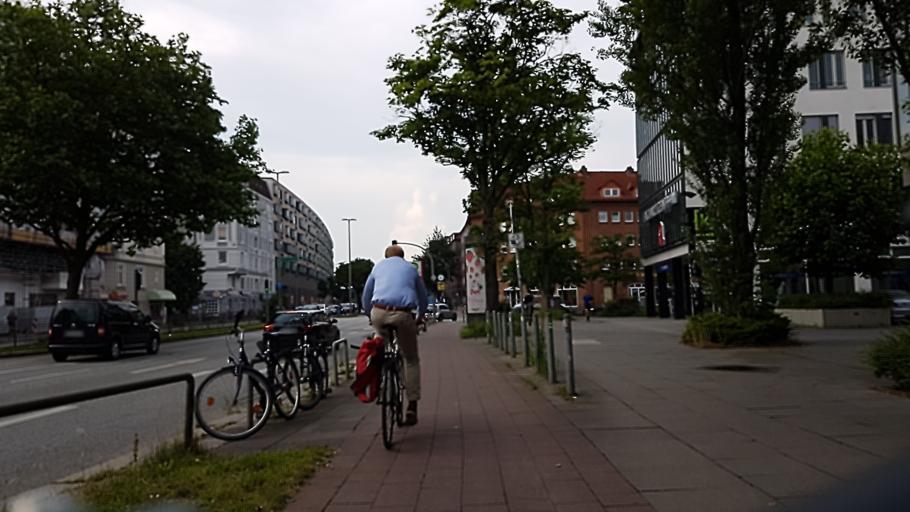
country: DE
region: Hamburg
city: Hamburg
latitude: 53.5831
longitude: 10.0195
